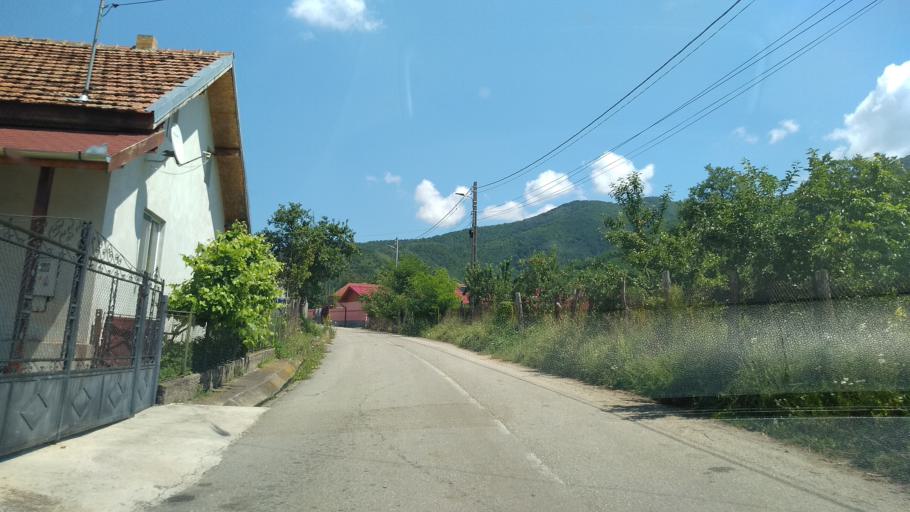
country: RO
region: Hunedoara
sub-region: Comuna Santamaria-Orlea
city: Santamaria-Orlea
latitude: 45.6006
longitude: 23.0146
